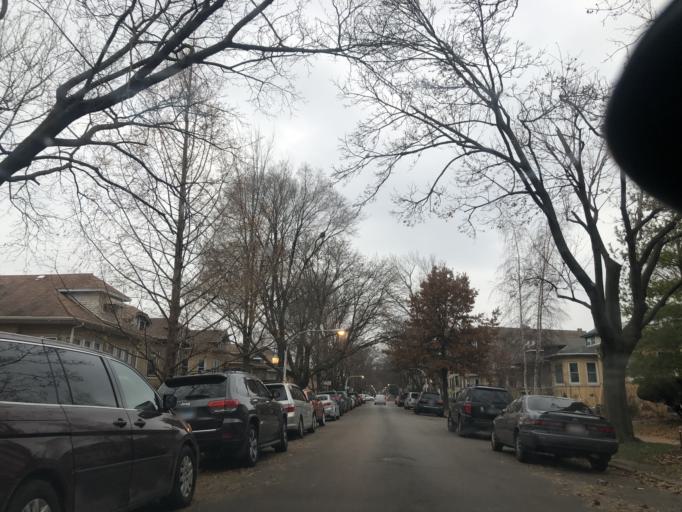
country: US
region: Illinois
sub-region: Cook County
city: Lincolnwood
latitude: 41.9953
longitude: -87.6947
